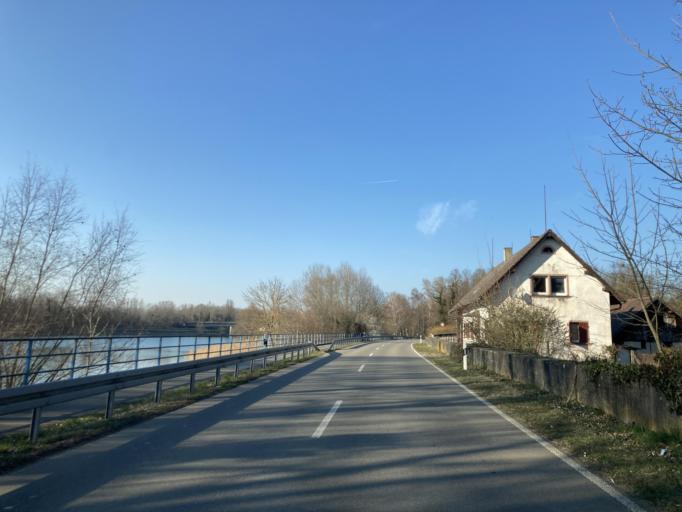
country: DE
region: Baden-Wuerttemberg
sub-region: Freiburg Region
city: Sasbach
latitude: 48.1496
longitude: 7.6007
